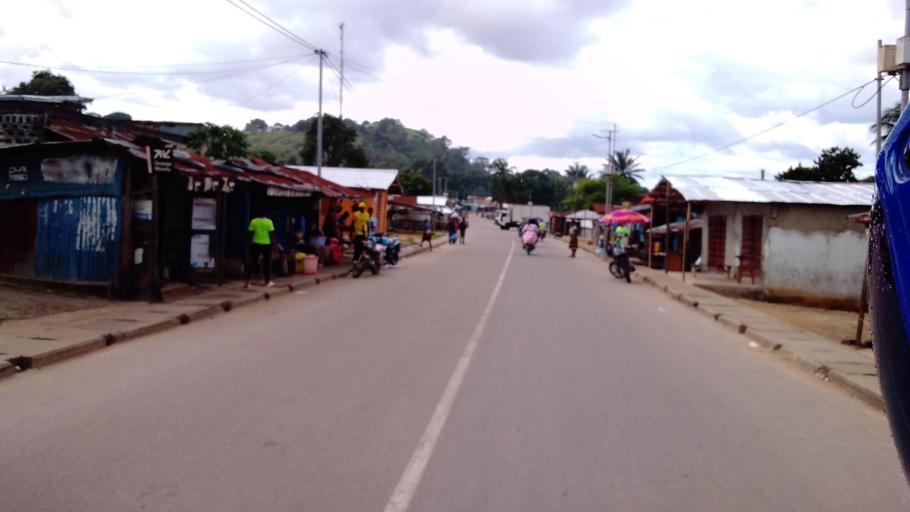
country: SL
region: Eastern Province
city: Koidu
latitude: 8.6470
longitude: -10.9744
